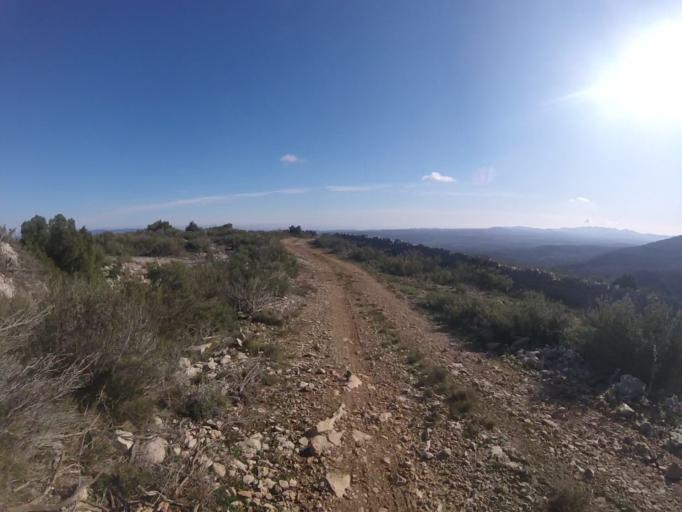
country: ES
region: Valencia
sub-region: Provincia de Castello
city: Sarratella
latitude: 40.3002
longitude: 0.0420
